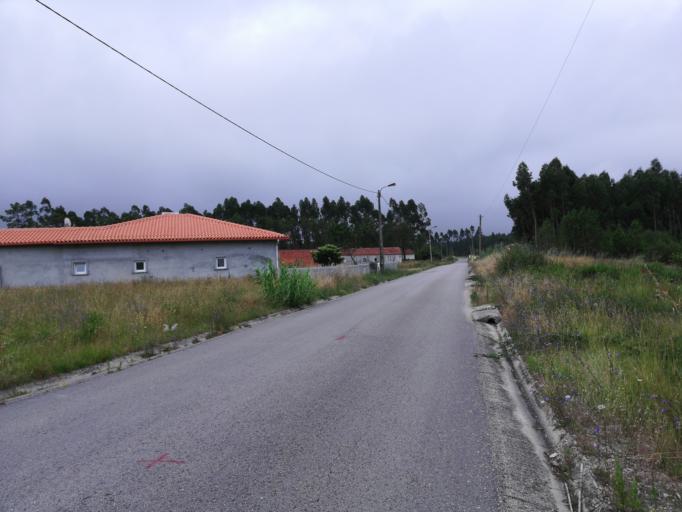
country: PT
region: Coimbra
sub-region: Mira
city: Mira
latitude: 40.4581
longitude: -8.6374
